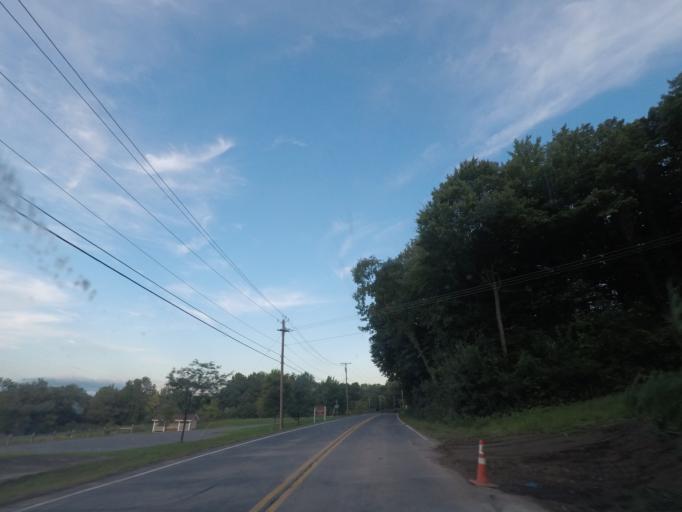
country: US
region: New York
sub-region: Schenectady County
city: Niskayuna
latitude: 42.7718
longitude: -73.8154
